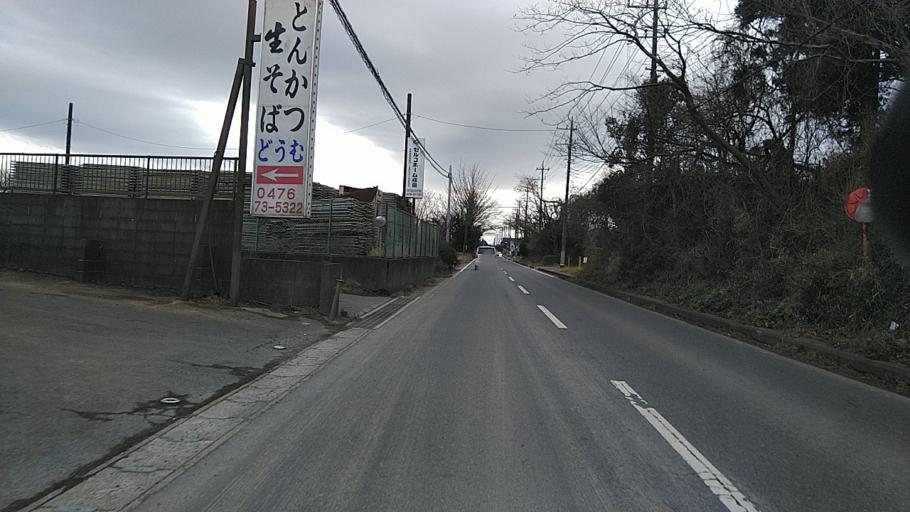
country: JP
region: Chiba
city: Sawara
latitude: 35.8378
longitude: 140.4557
